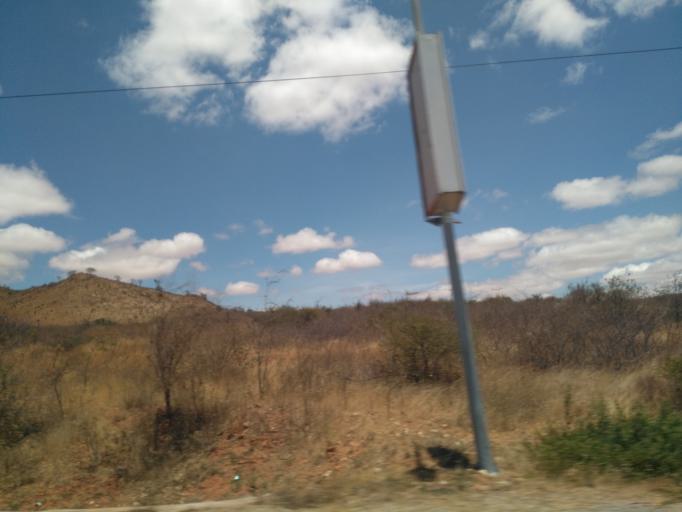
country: TZ
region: Dodoma
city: Kisasa
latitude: -6.2222
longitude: 35.7812
